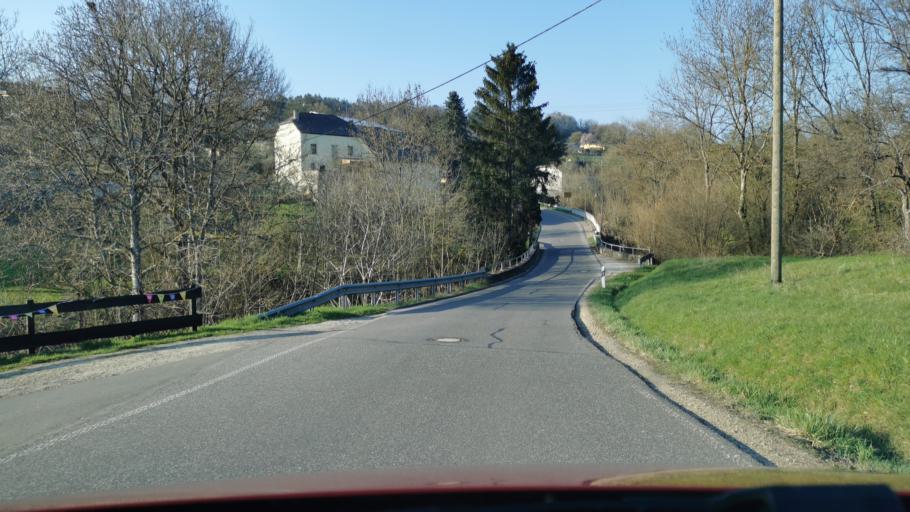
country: DE
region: Rheinland-Pfalz
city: Trierweiler
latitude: 49.7758
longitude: 6.5486
